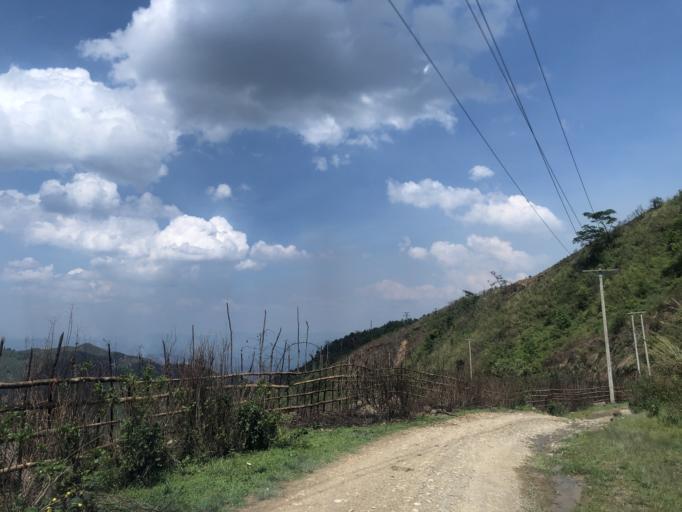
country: LA
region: Phongsali
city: Phongsali
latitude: 21.3966
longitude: 102.2169
